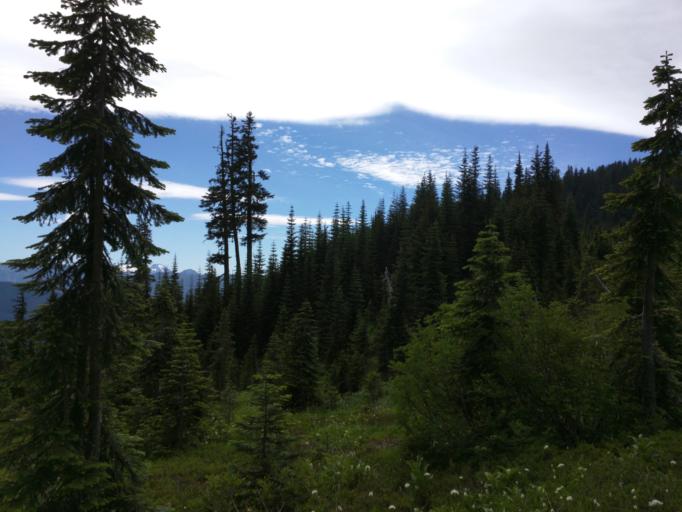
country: CA
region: British Columbia
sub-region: Fraser Valley Regional District
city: Chilliwack
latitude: 48.9274
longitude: -121.8609
